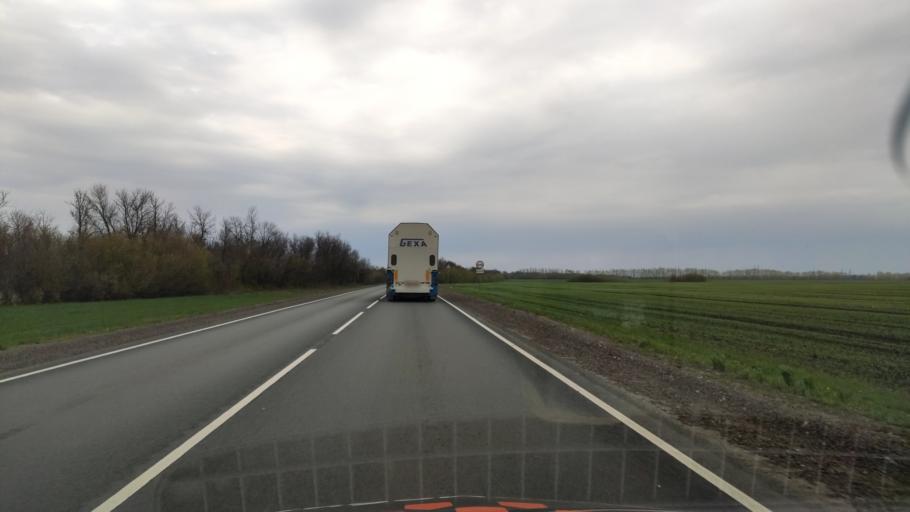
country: RU
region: Voronezj
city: Nizhnedevitsk
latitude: 51.6075
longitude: 38.6094
